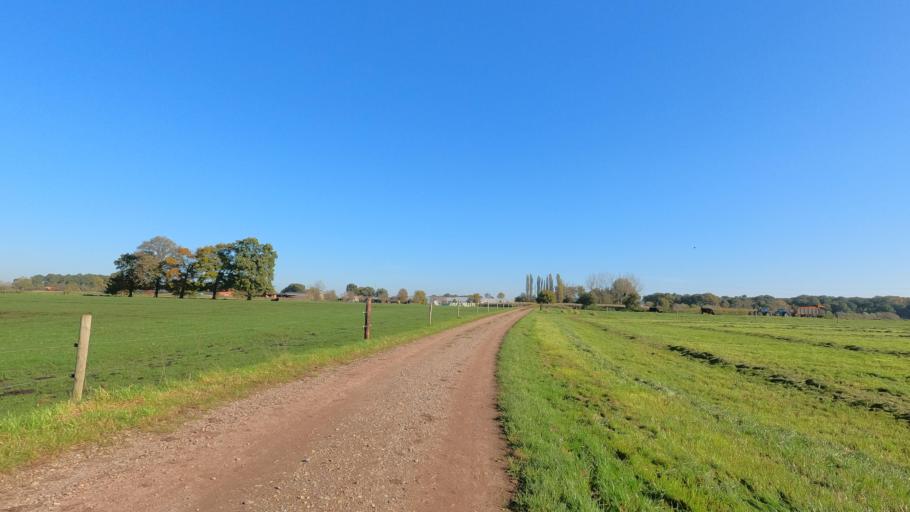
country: BE
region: Flanders
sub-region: Provincie Antwerpen
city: Oostmalle
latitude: 51.3026
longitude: 4.7033
